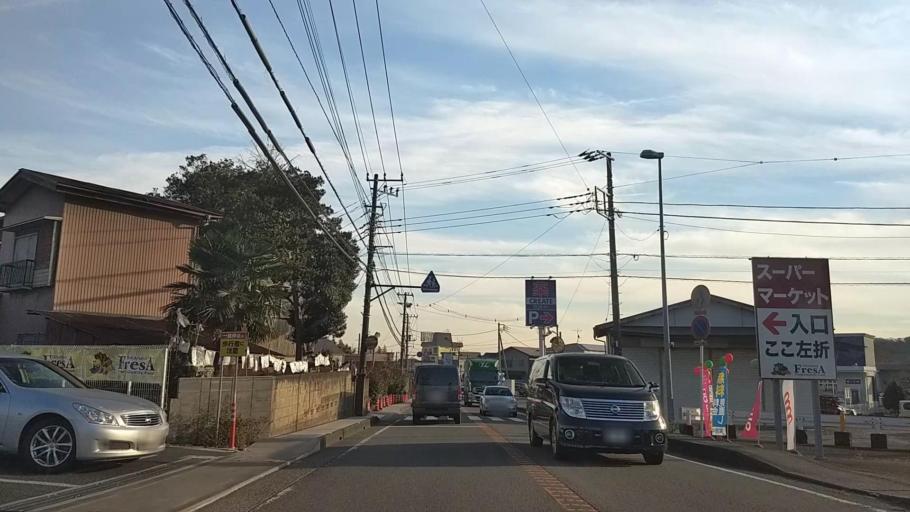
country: JP
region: Kanagawa
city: Atsugi
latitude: 35.4970
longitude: 139.3152
